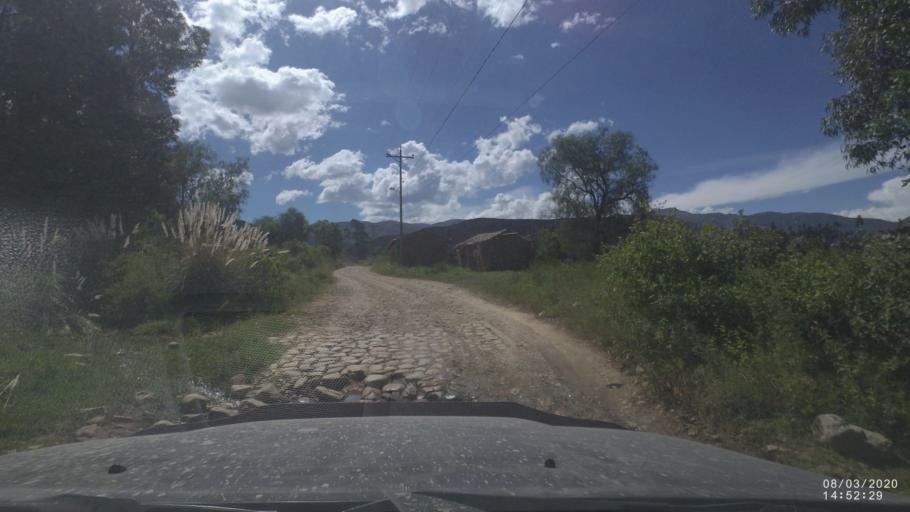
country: BO
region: Cochabamba
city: Totora
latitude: -17.6822
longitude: -65.3518
